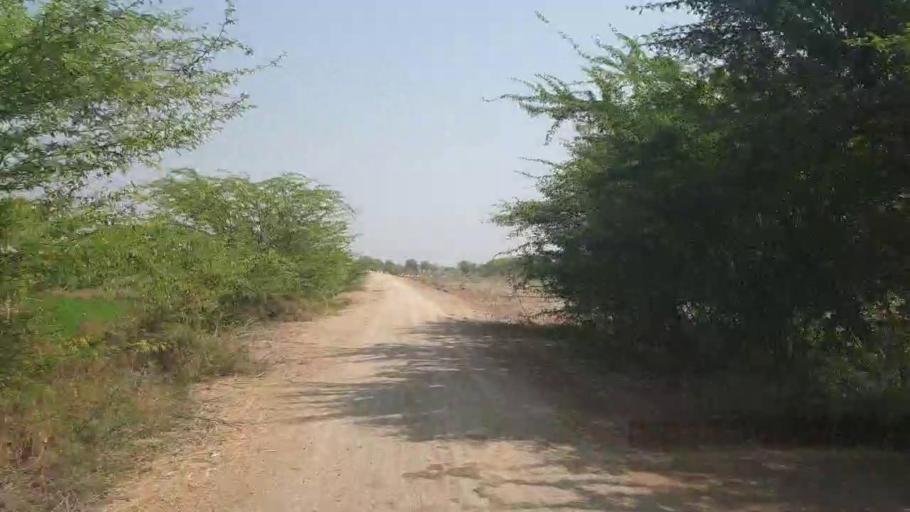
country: PK
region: Sindh
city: Umarkot
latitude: 25.4437
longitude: 69.6634
